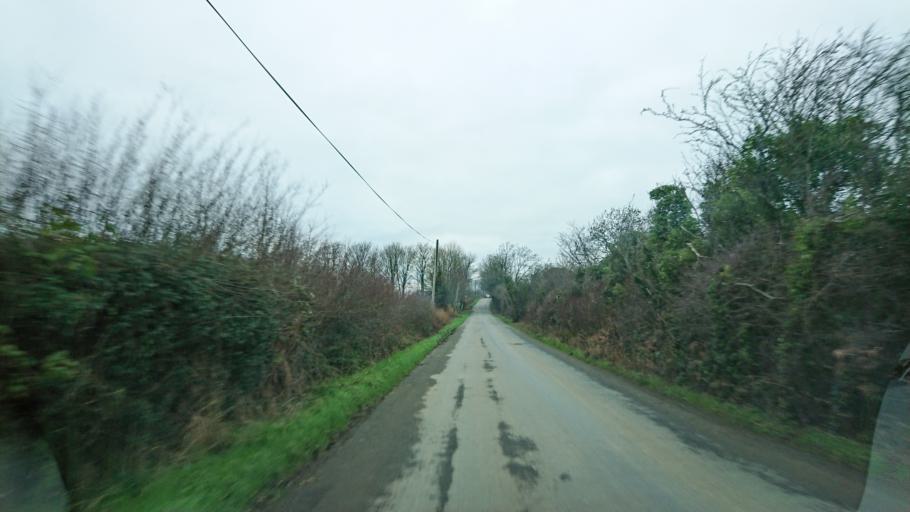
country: IE
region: Munster
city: Carrick-on-Suir
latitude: 52.2759
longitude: -7.4201
